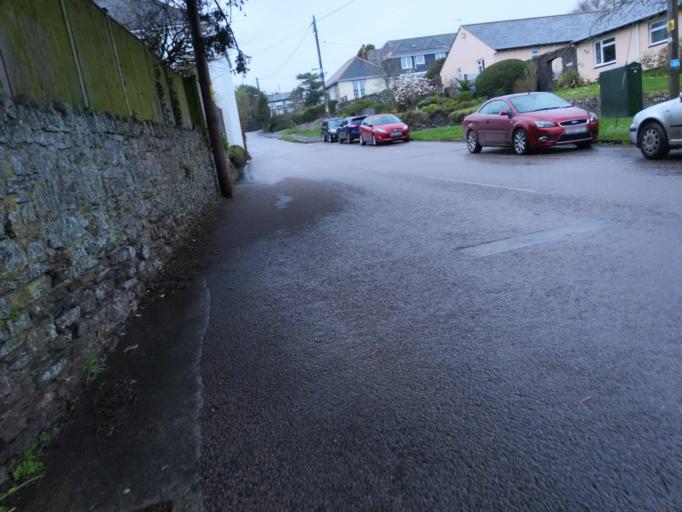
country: GB
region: England
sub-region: Devon
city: Wembury
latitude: 50.3169
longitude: -4.0362
